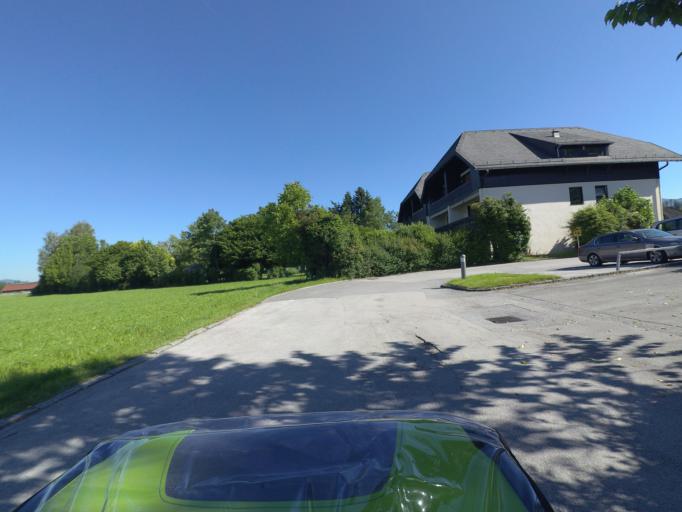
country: AT
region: Salzburg
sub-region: Politischer Bezirk Salzburg-Umgebung
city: Anif
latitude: 47.7490
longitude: 13.0580
